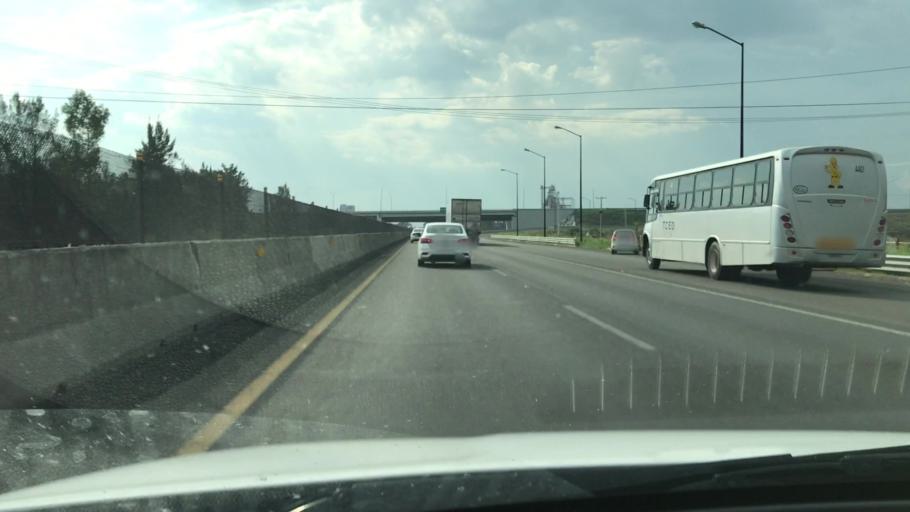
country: MX
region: Guanajuato
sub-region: Salamanca
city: San Vicente de Flores
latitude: 20.5965
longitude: -101.2368
